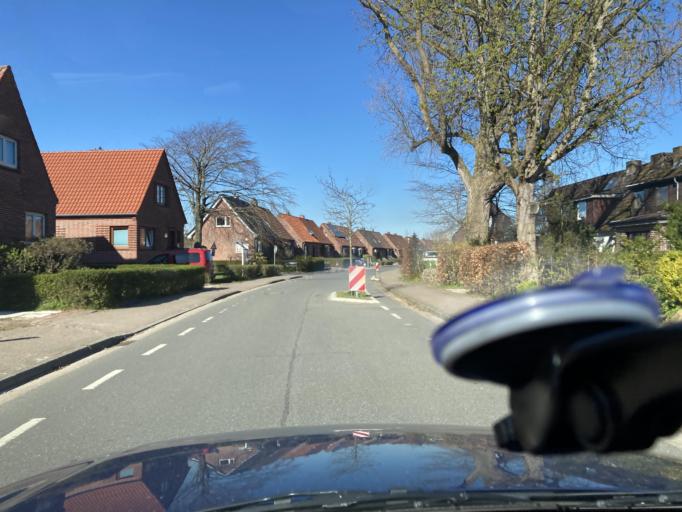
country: DE
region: Schleswig-Holstein
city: Busum
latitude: 54.1342
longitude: 8.8565
